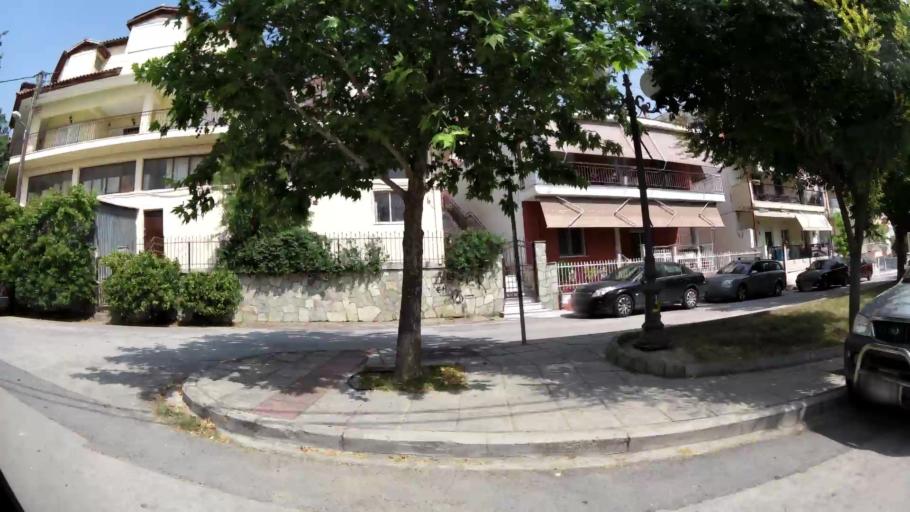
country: GR
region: Central Macedonia
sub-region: Nomos Thessalonikis
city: Efkarpia
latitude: 40.6909
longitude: 22.9536
